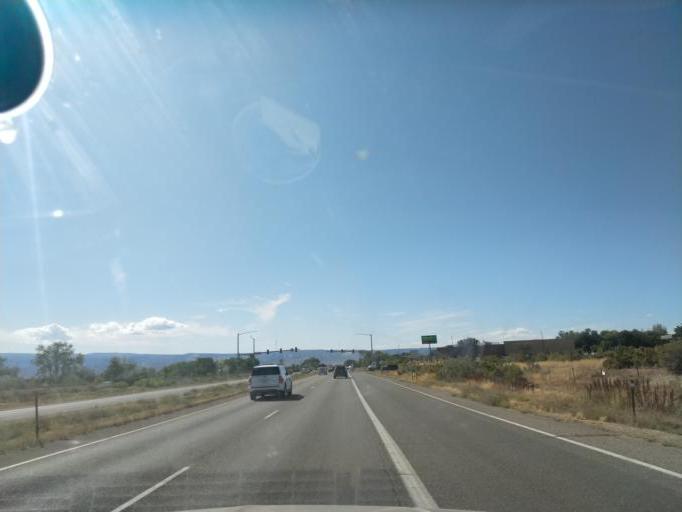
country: US
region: Colorado
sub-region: Mesa County
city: Clifton
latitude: 39.0834
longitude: -108.4711
